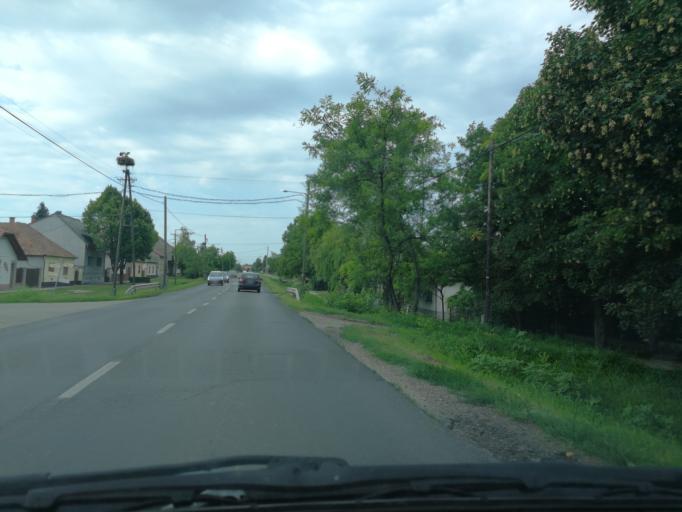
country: HU
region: Bacs-Kiskun
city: Sukosd
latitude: 46.2845
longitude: 18.9910
